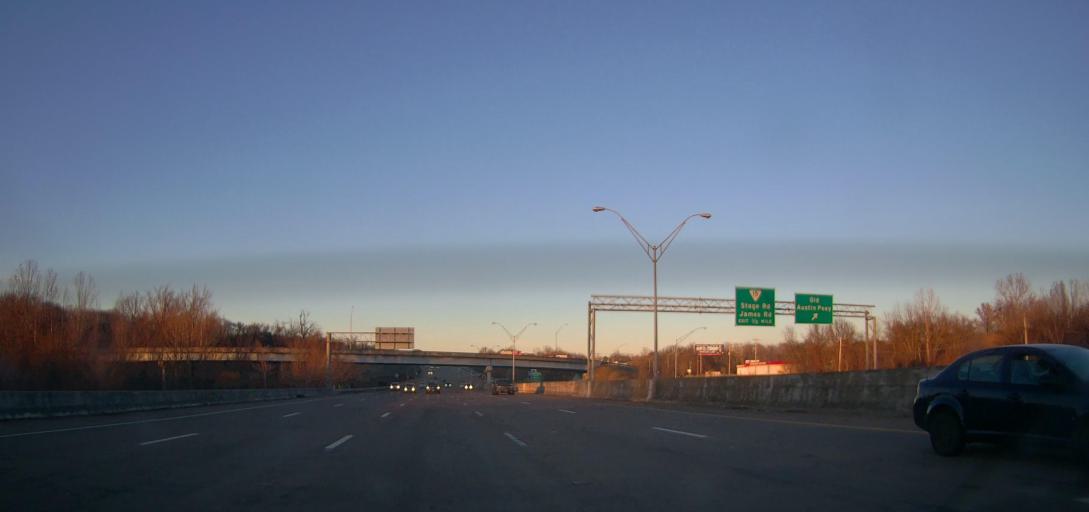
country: US
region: Tennessee
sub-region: Shelby County
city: Bartlett
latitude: 35.1971
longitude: -89.9254
